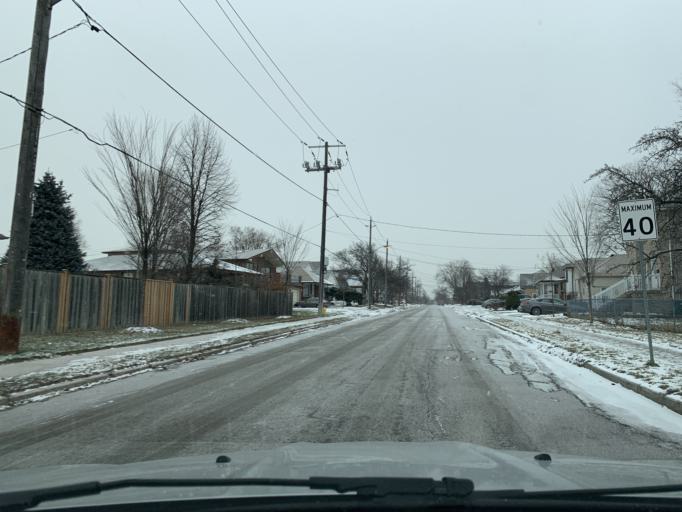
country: CA
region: Ontario
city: Toronto
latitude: 43.7304
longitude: -79.4720
